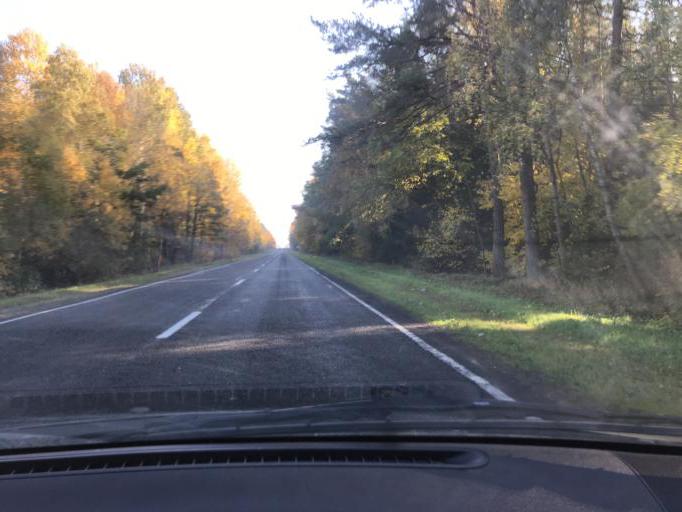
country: BY
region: Brest
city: Lyakhavichy
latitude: 52.9531
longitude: 26.2270
